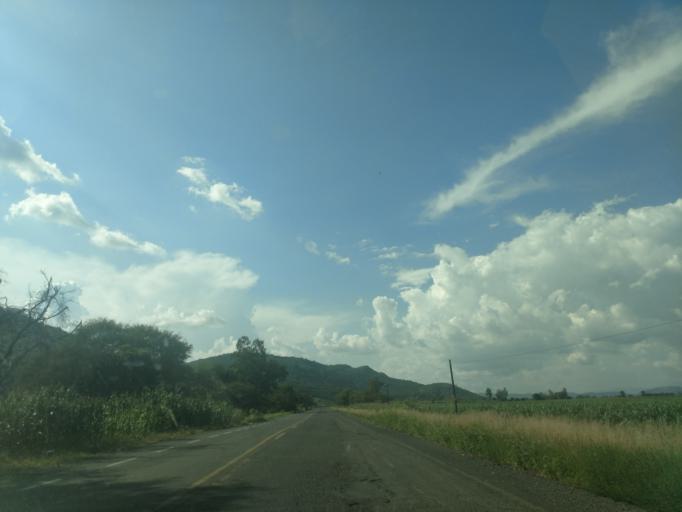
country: MX
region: Jalisco
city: Antonio Escobedo
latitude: 20.8538
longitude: -104.0288
